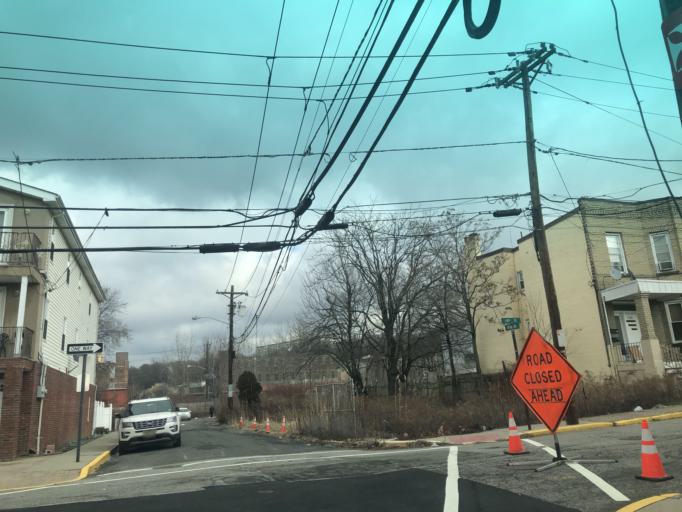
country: US
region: New Jersey
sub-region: Hudson County
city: Union City
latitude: 40.7850
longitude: -74.0297
